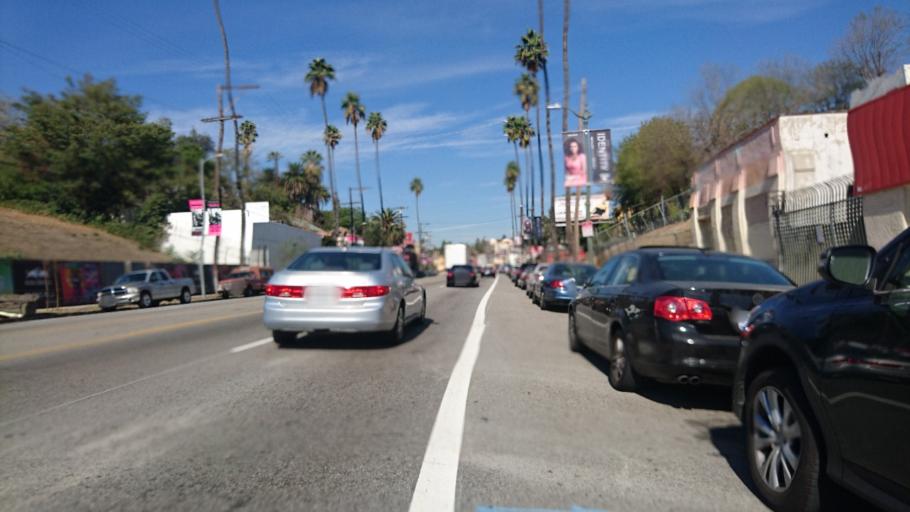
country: US
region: California
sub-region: Los Angeles County
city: Echo Park
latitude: 34.0693
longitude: -118.2504
